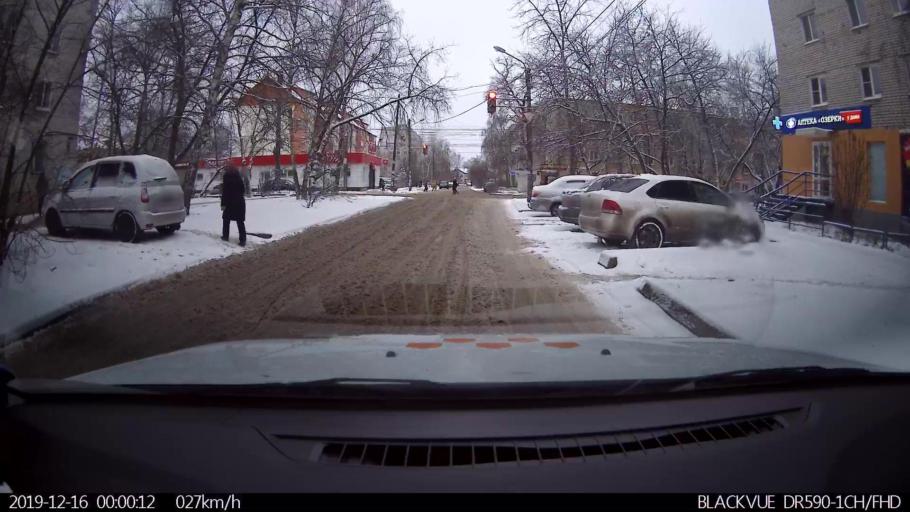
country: RU
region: Nizjnij Novgorod
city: Neklyudovo
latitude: 56.3600
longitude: 43.8490
